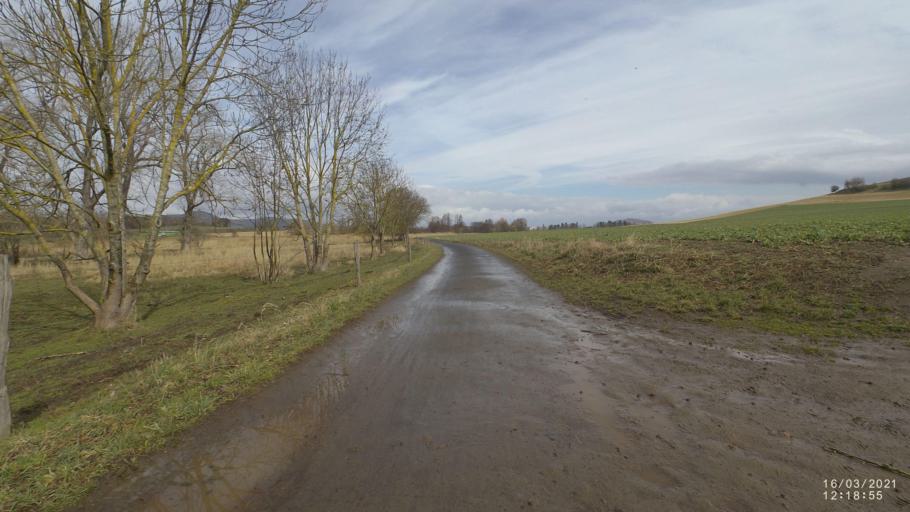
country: DE
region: Rheinland-Pfalz
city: Thur
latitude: 50.3534
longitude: 7.2880
